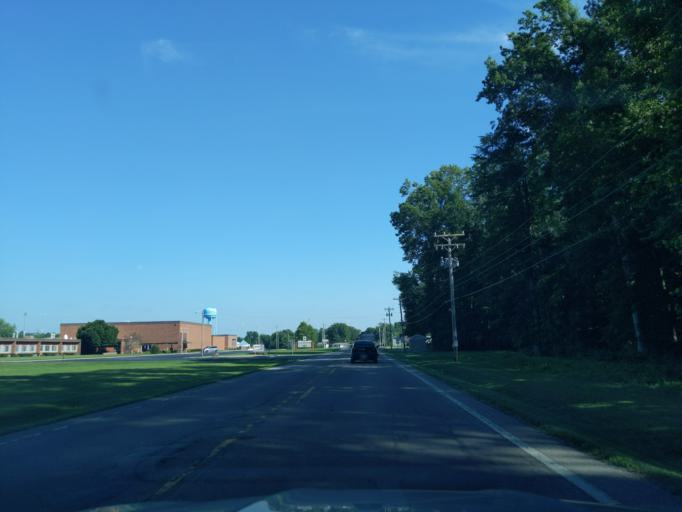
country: US
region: Indiana
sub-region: Ripley County
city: Osgood
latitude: 39.1429
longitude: -85.2970
